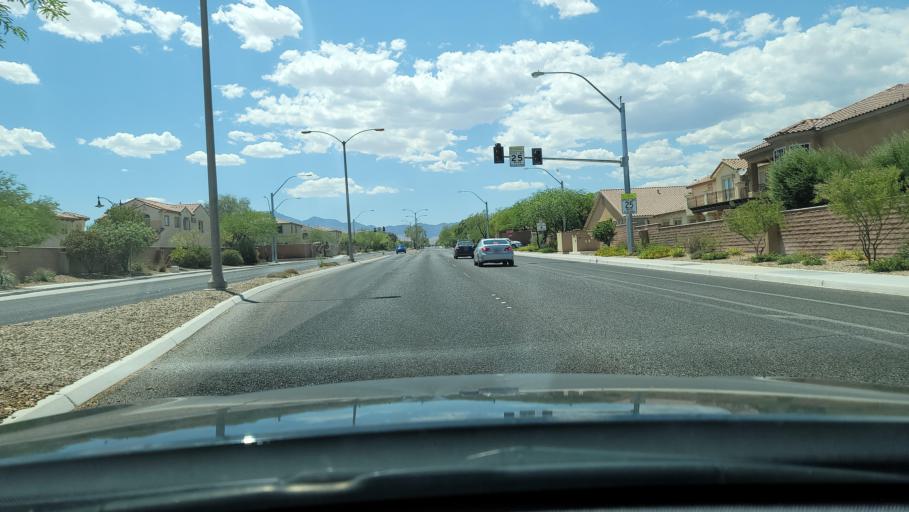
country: US
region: Nevada
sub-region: Clark County
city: Enterprise
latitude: 36.0123
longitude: -115.2696
